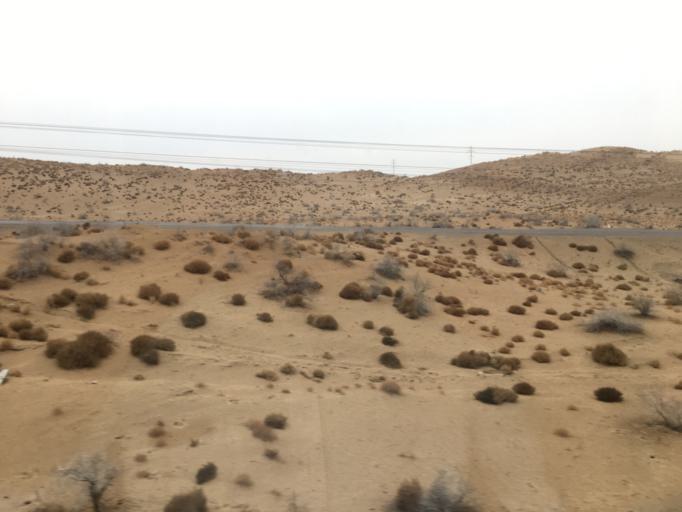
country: TM
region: Mary
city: Yoloeten
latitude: 36.4441
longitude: 62.5871
